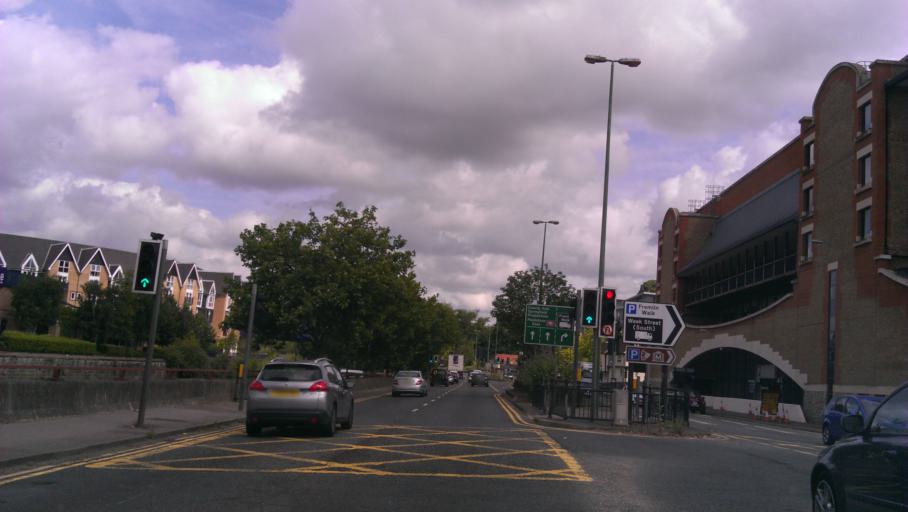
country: GB
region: England
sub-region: Kent
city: Maidstone
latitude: 51.2741
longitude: 0.5184
